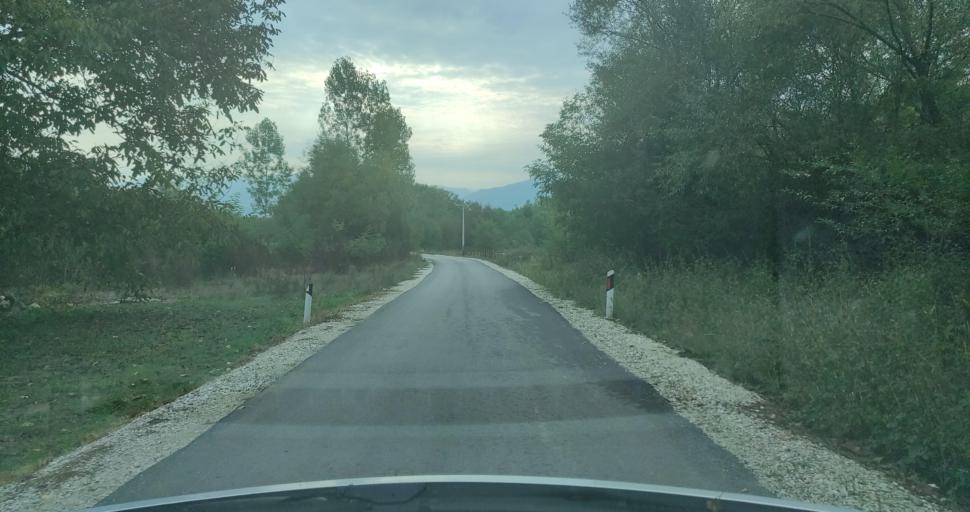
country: RS
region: Central Serbia
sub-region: Pcinjski Okrug
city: Vladicin Han
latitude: 42.6712
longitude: 22.0233
